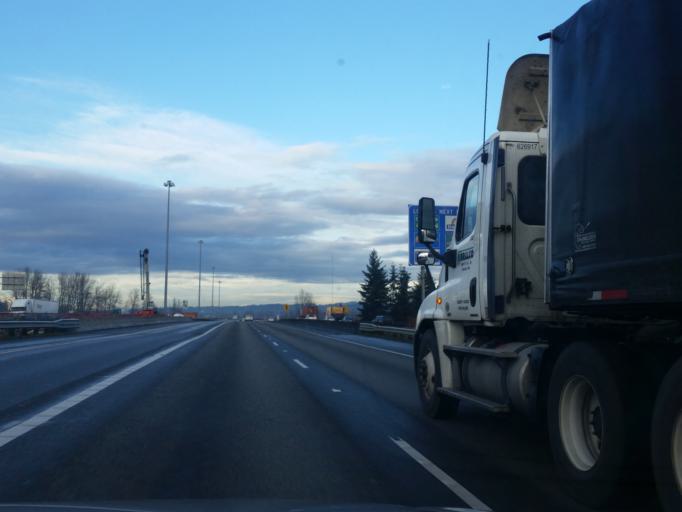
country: US
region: Washington
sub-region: King County
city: Algona
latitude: 47.3016
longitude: -122.2530
